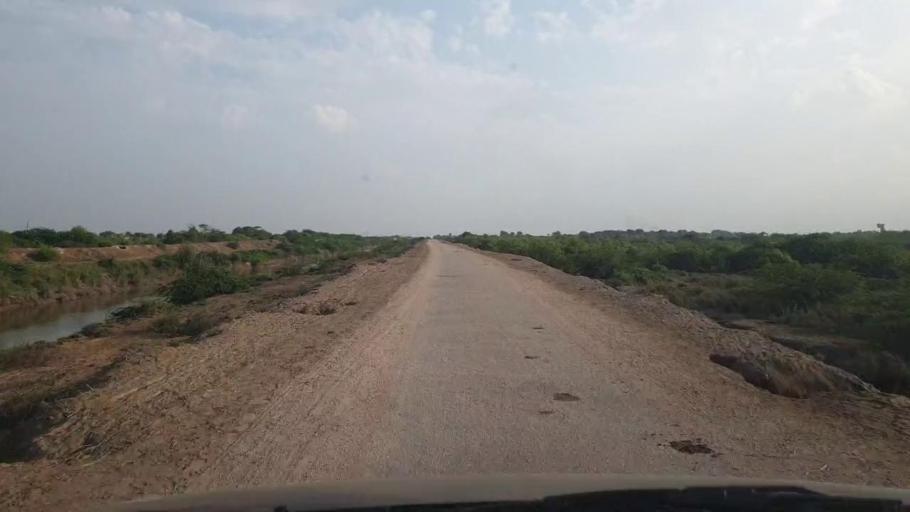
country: PK
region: Sindh
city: Badin
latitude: 24.5365
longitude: 68.6761
